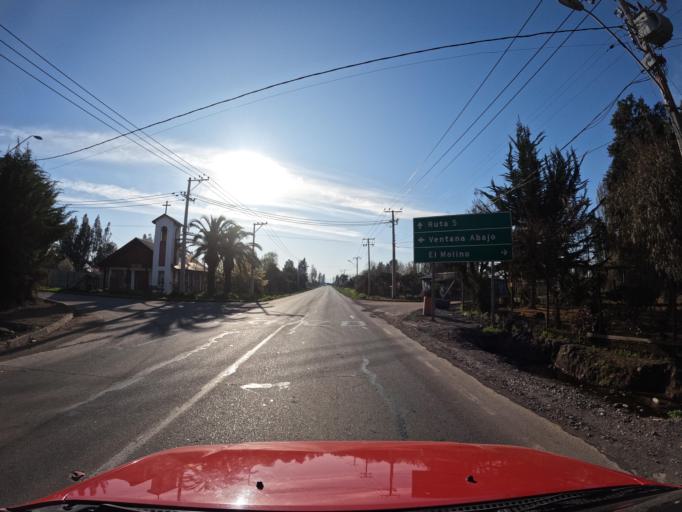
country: CL
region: Maule
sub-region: Provincia de Curico
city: Teno
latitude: -34.9052
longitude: -71.0514
